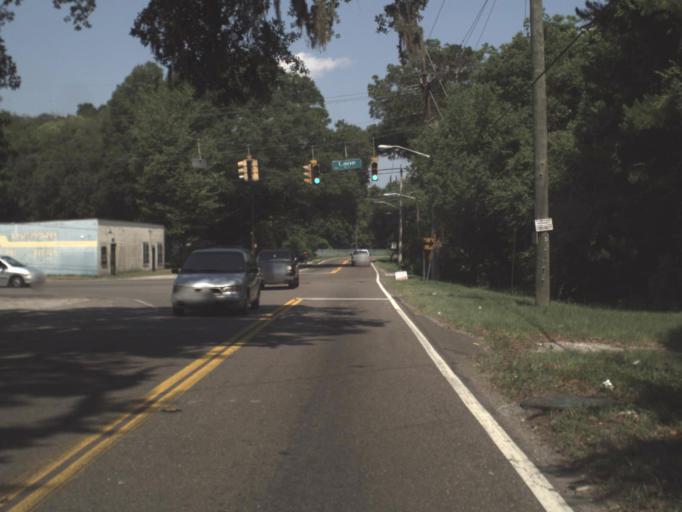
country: US
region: Florida
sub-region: Duval County
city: Jacksonville
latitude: 30.3656
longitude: -81.7411
